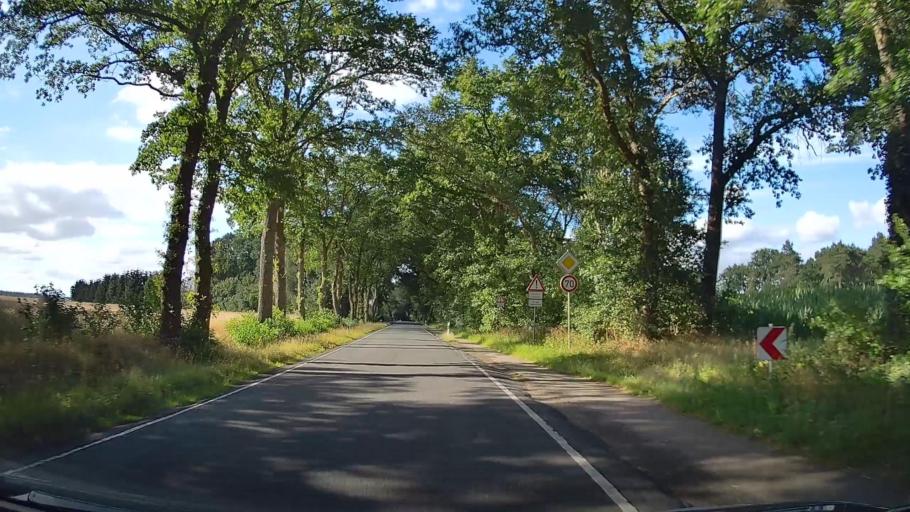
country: DE
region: Lower Saxony
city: Molbergen
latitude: 52.9357
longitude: 7.8956
